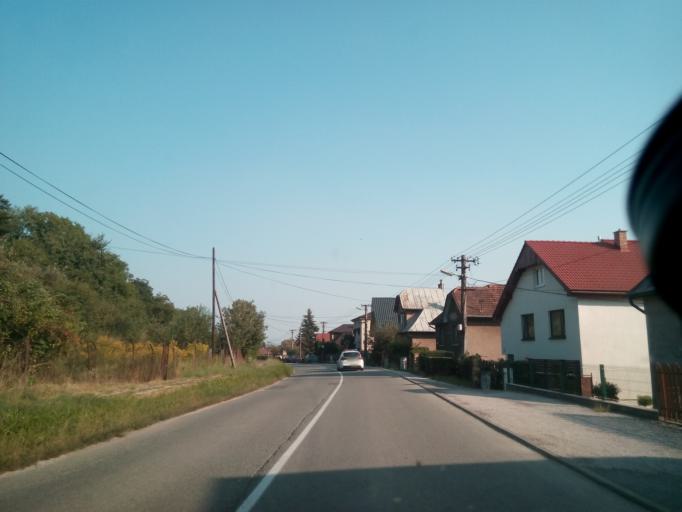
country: SK
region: Kosicky
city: Kosice
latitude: 48.7133
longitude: 21.1983
